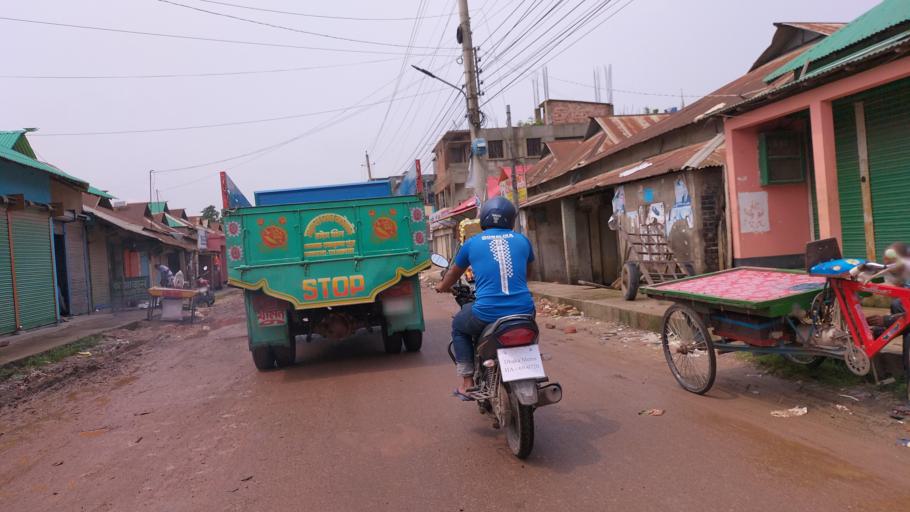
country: BD
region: Dhaka
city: Netrakona
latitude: 24.8906
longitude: 90.7386
